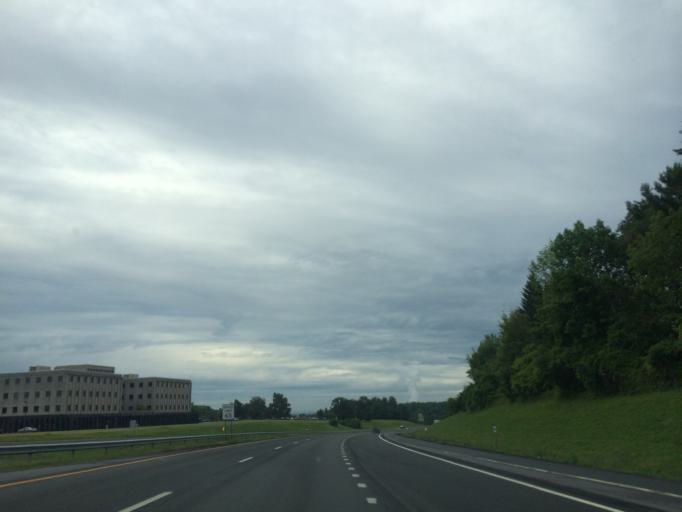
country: US
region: New York
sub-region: Albany County
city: Albany
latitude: 42.6312
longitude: -73.7801
